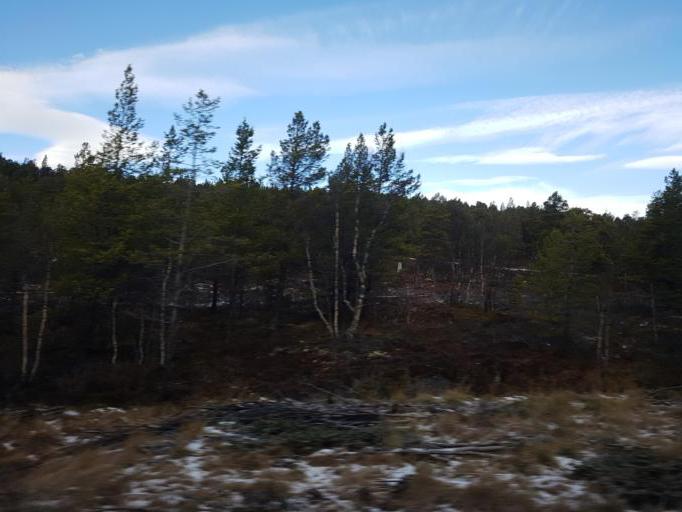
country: NO
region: Oppland
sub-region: Dovre
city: Dombas
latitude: 62.1077
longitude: 9.1926
